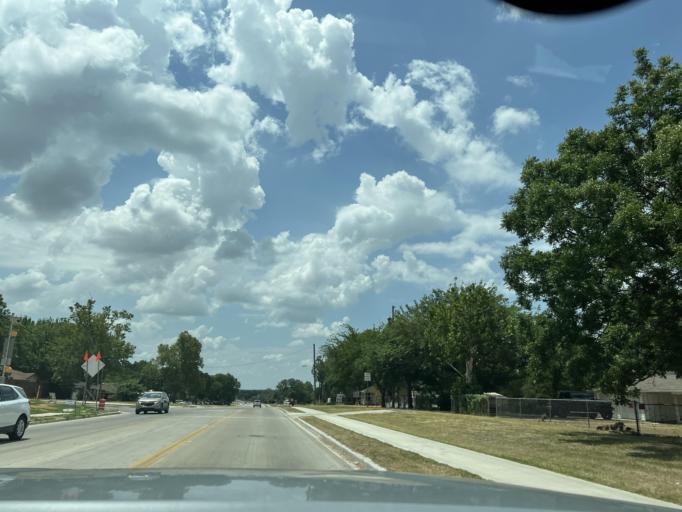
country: US
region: Texas
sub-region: Parker County
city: Springtown
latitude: 32.9785
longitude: -97.6862
